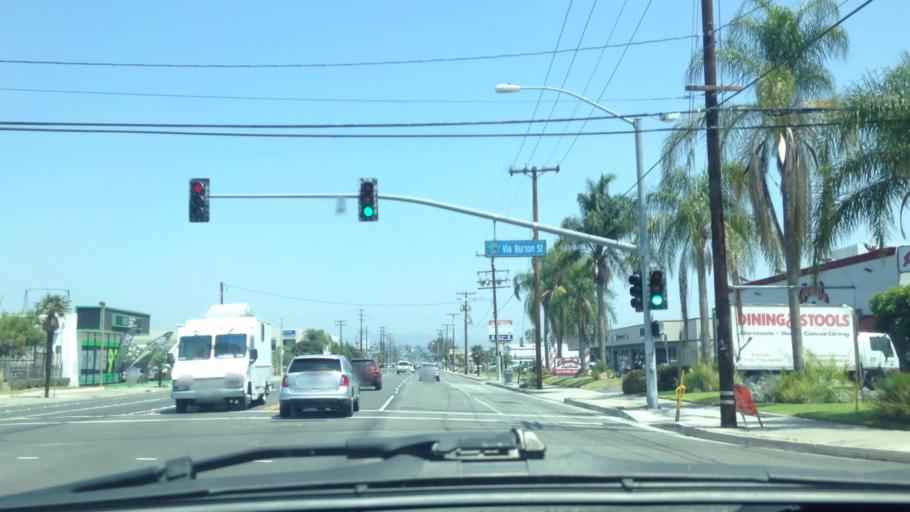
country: US
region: California
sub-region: Orange County
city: Placentia
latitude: 33.8562
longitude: -117.8893
